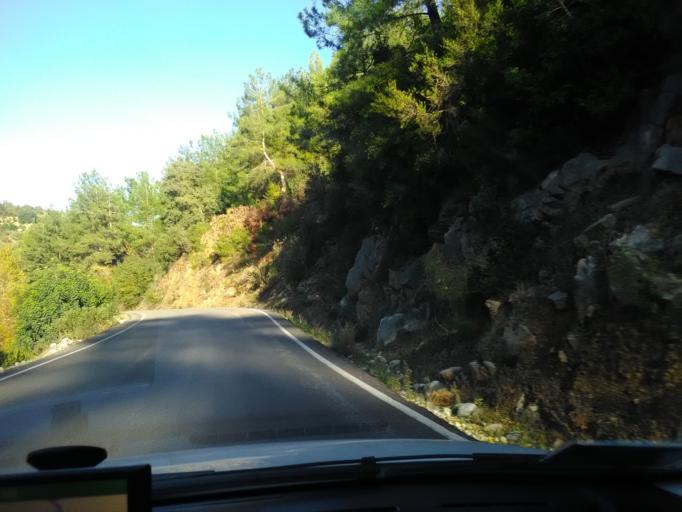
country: TR
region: Antalya
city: Gazipasa
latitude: 36.2826
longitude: 32.3660
